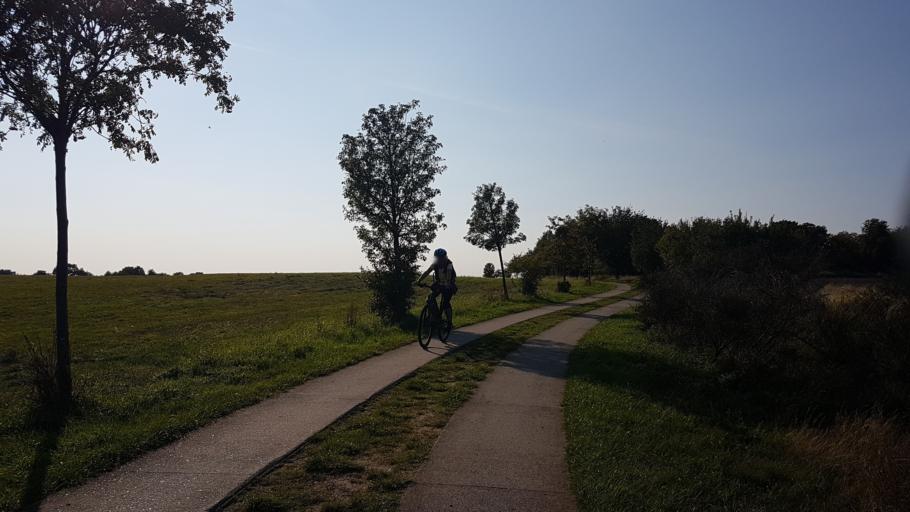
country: DE
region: Mecklenburg-Vorpommern
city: Ostseebad Sellin
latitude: 54.3551
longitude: 13.6763
